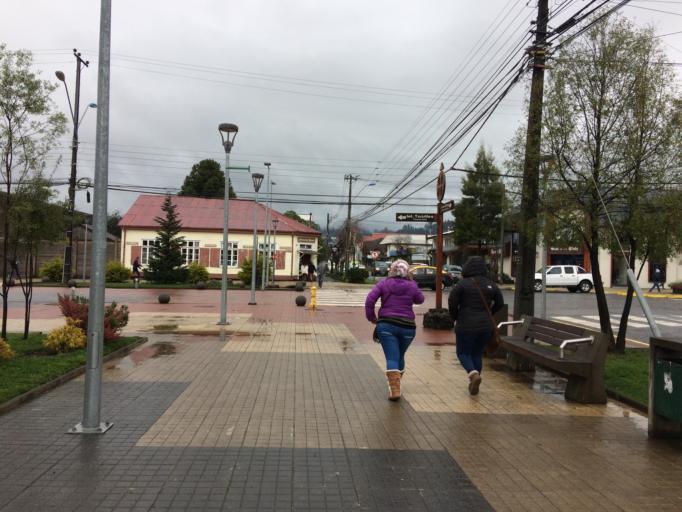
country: CL
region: Araucania
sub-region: Provincia de Cautin
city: Villarrica
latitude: -39.2834
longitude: -72.2268
